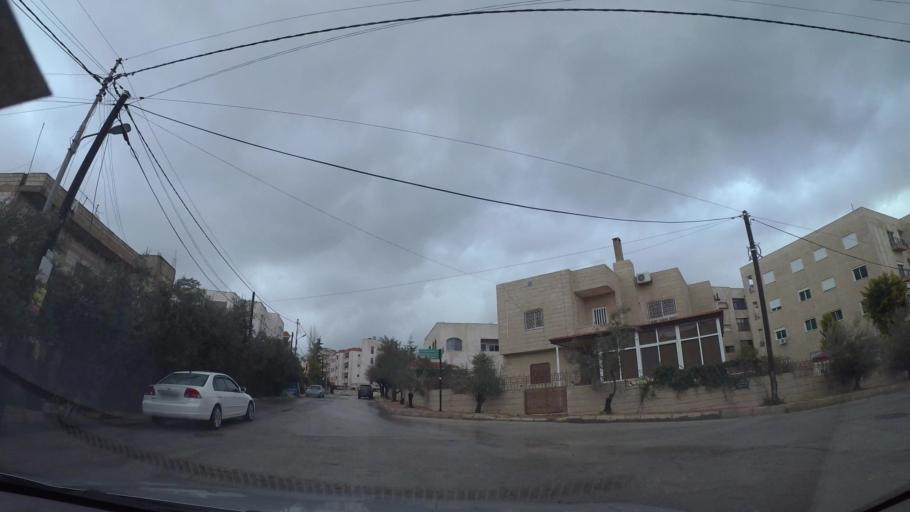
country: JO
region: Amman
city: Al Jubayhah
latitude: 32.0356
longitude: 35.8668
